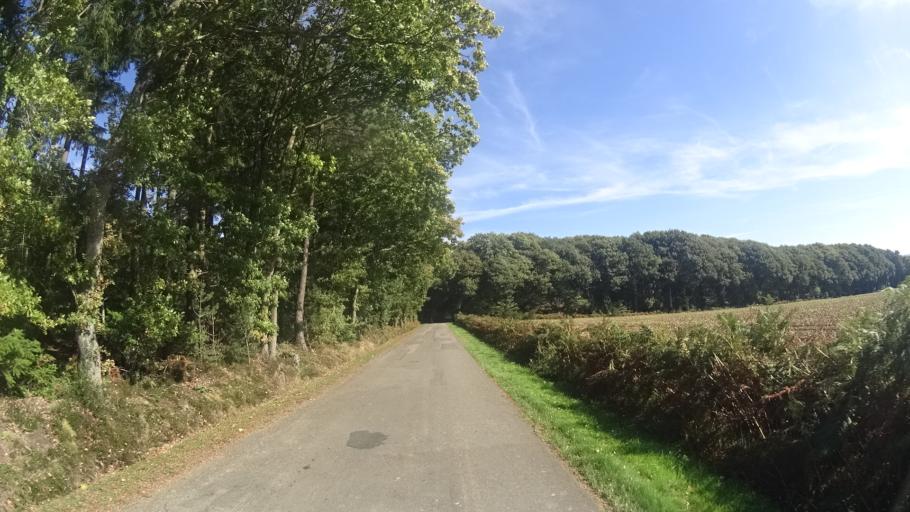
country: FR
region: Brittany
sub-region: Departement du Morbihan
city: La Gacilly
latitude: 47.7469
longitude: -2.1653
